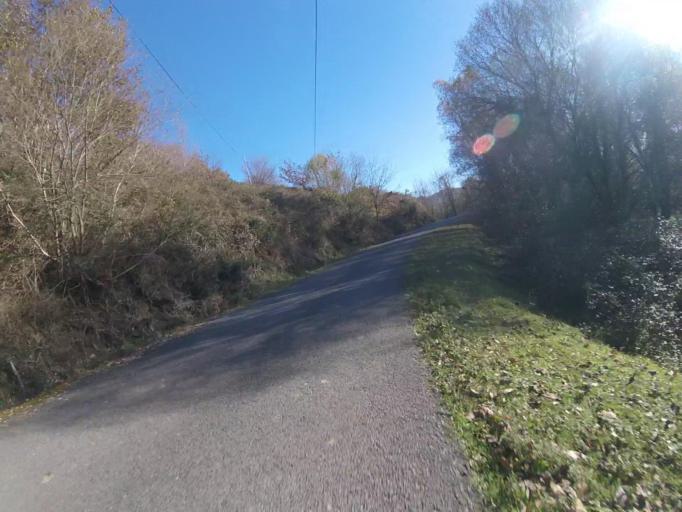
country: ES
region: Navarre
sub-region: Provincia de Navarra
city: Bera
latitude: 43.2968
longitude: -1.6534
